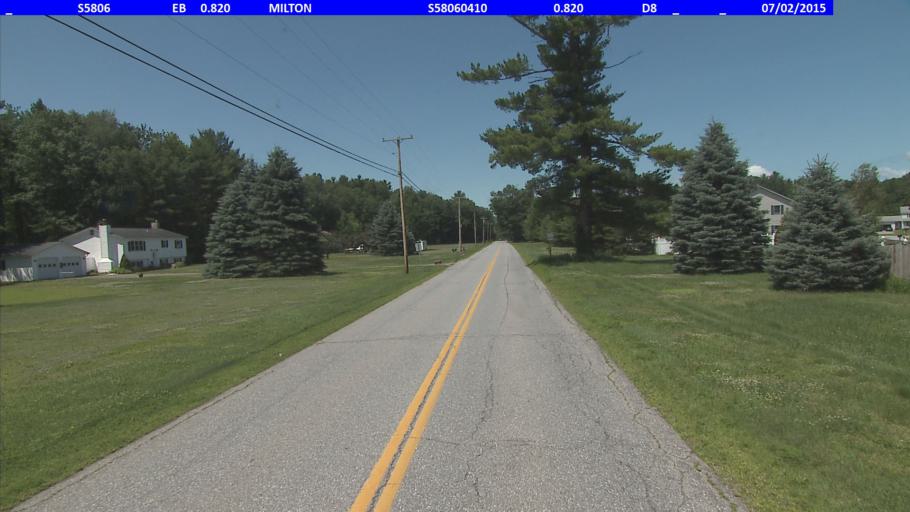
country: US
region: Vermont
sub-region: Chittenden County
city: Milton
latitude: 44.6589
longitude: -73.1268
